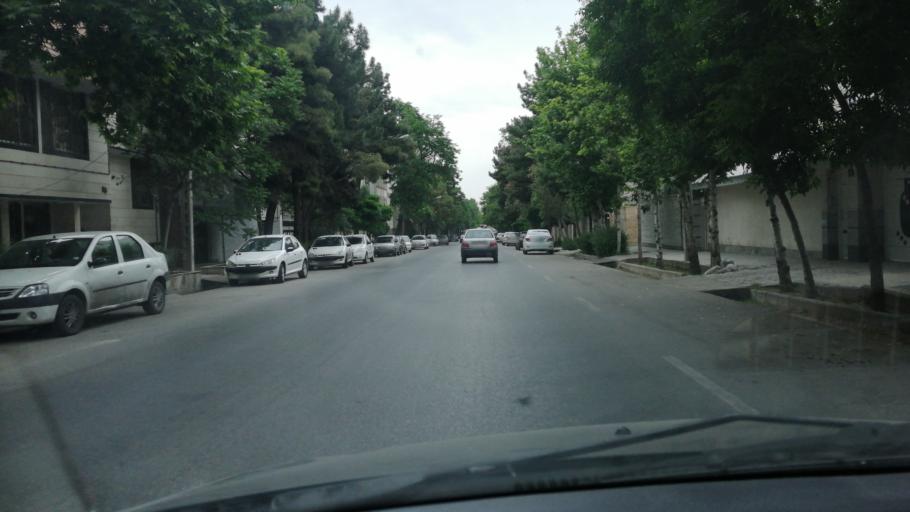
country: IR
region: Razavi Khorasan
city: Mashhad
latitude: 36.2832
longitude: 59.5721
